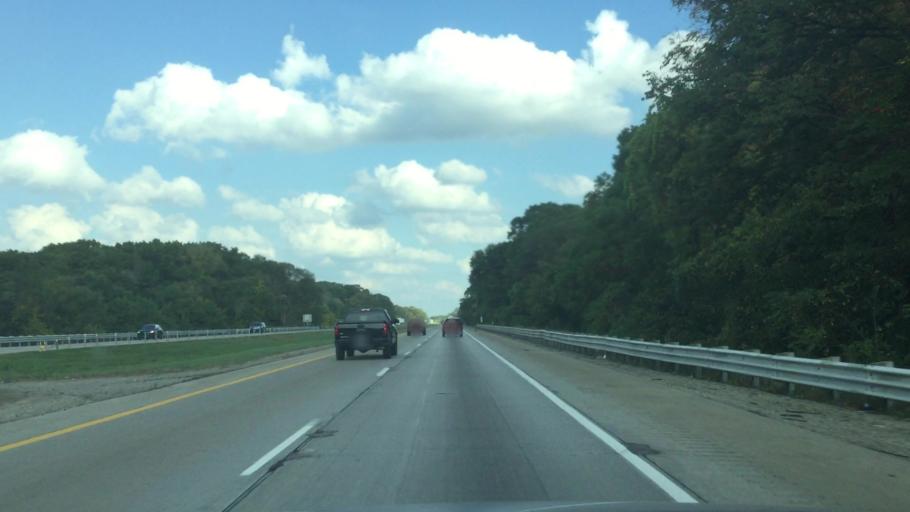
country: US
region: Michigan
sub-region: Calhoun County
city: Brownlee Park
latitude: 42.2852
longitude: -85.1441
